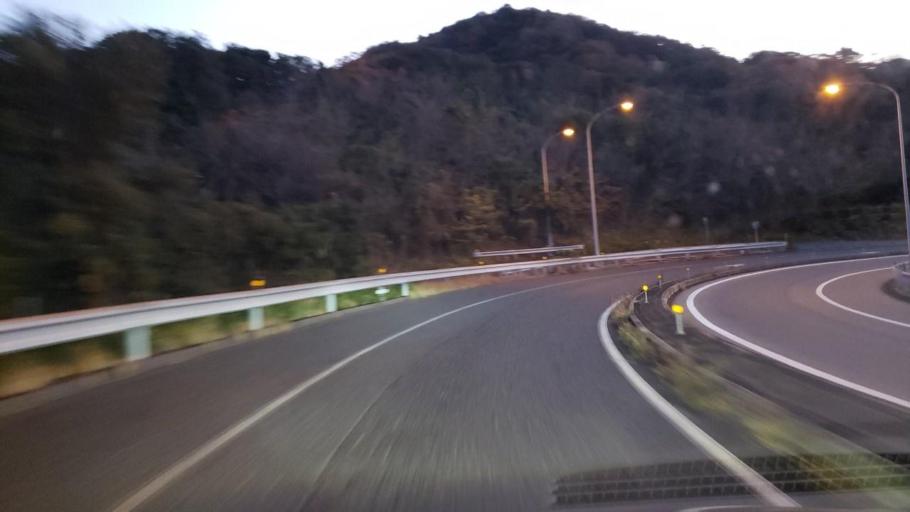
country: JP
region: Hyogo
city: Fukura
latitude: 34.2587
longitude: 134.6844
